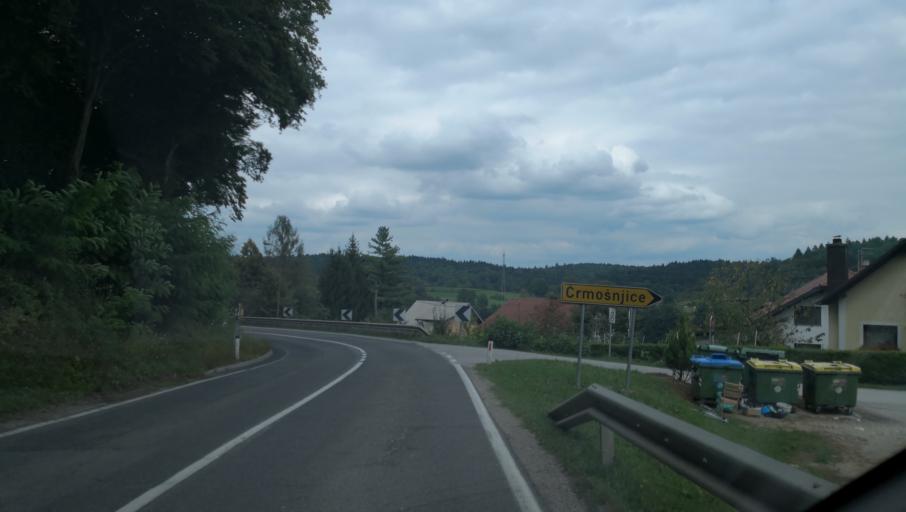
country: SI
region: Novo Mesto
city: Novo Mesto
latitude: 45.7739
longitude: 15.1875
